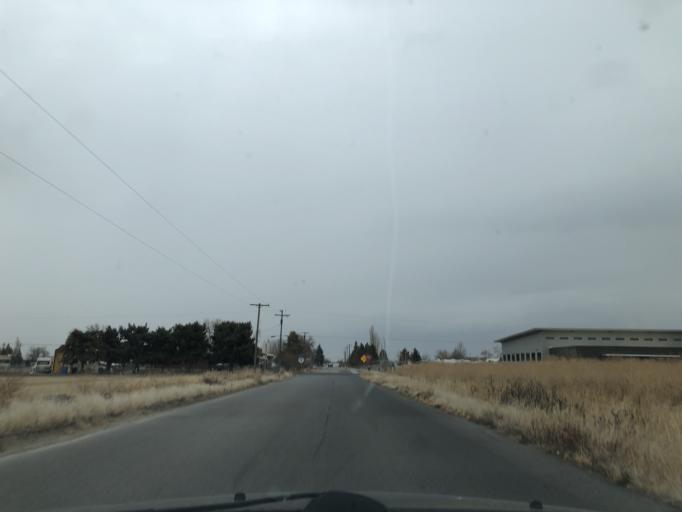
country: US
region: Utah
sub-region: Cache County
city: Nibley
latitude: 41.6920
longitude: -111.8622
